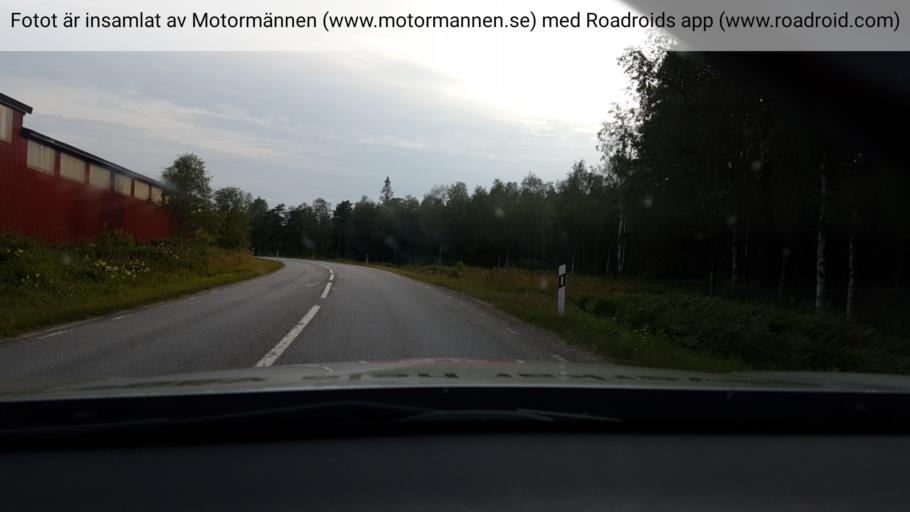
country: SE
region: Vaestra Goetaland
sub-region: Uddevalla Kommun
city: Uddevalla
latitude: 58.3746
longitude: 11.9786
